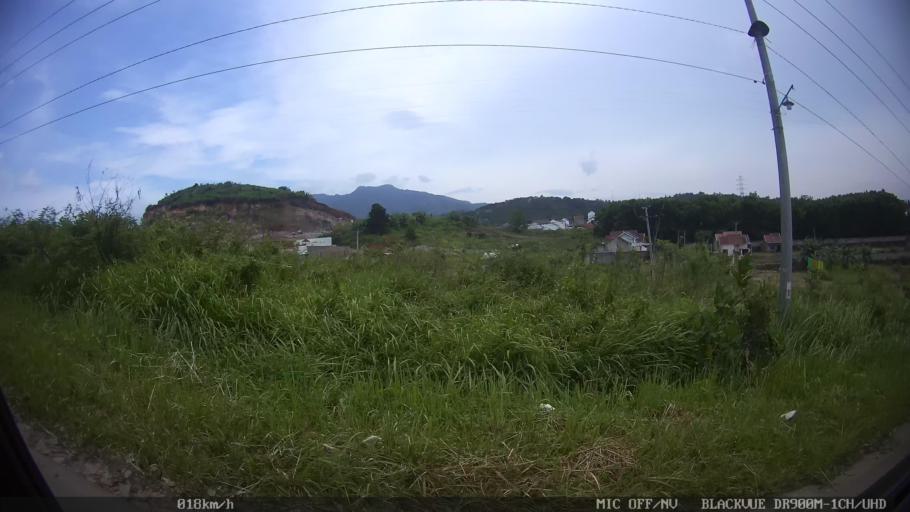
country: ID
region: Lampung
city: Bandarlampung
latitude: -5.4094
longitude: 105.1984
